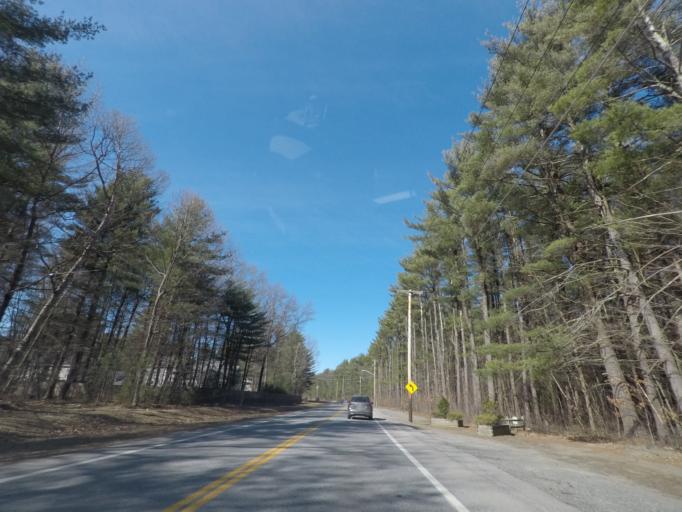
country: US
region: New York
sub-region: Saratoga County
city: North Ballston Spa
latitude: 43.0256
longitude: -73.8482
